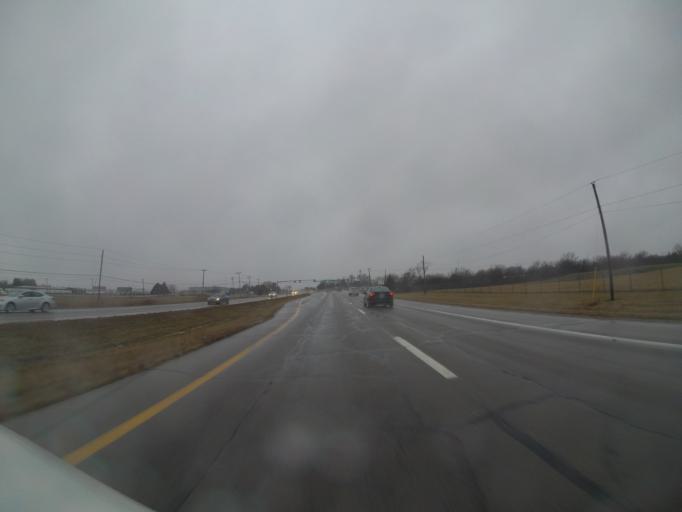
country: US
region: Ohio
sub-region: Wood County
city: Rossford
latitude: 41.5647
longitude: -83.5554
